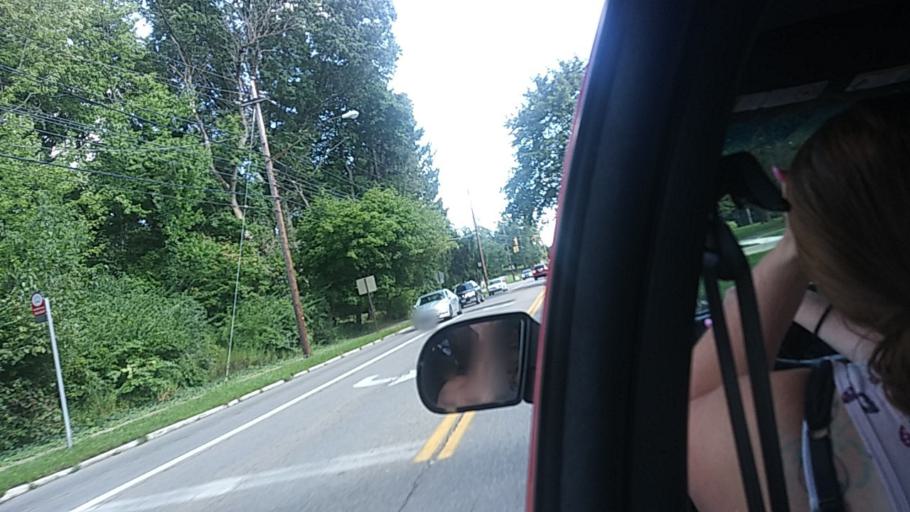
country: US
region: Ohio
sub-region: Summit County
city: Akron
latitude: 41.0995
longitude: -81.5560
